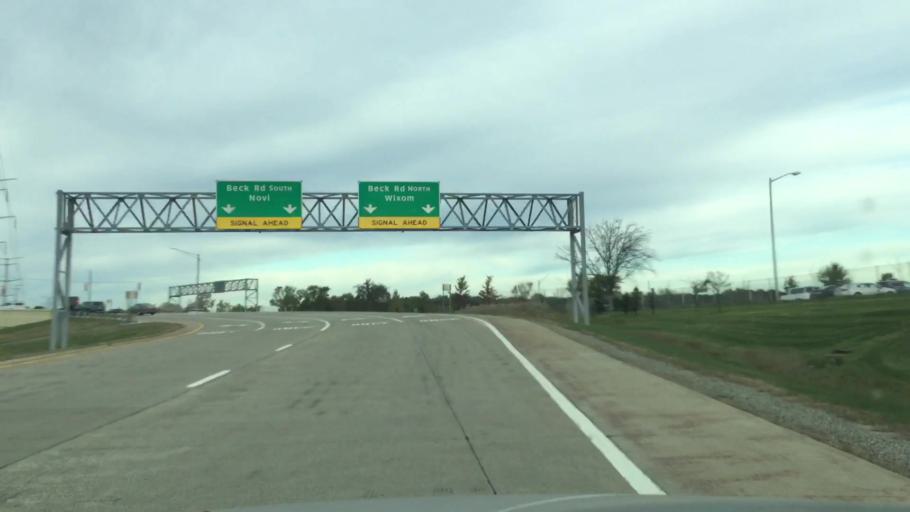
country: US
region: Michigan
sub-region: Oakland County
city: Wixom
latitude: 42.4939
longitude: -83.5135
